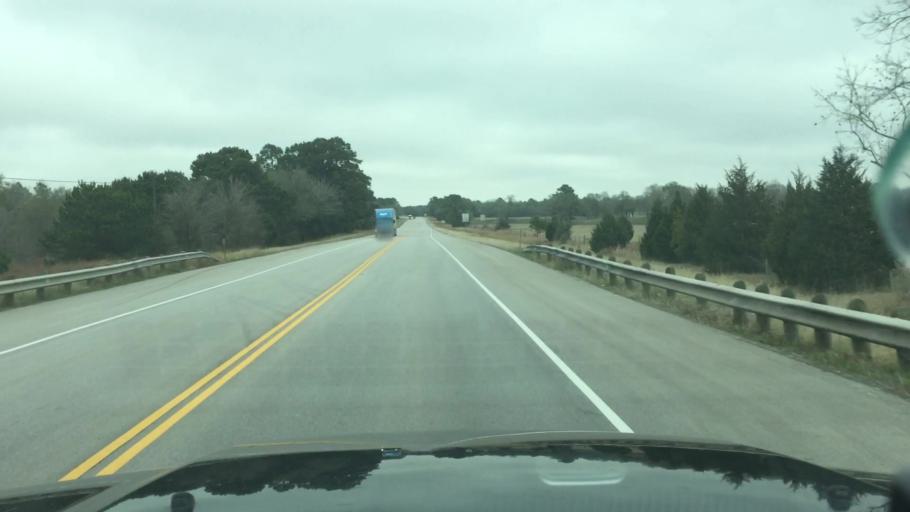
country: US
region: Texas
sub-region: Lee County
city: Giddings
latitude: 30.0848
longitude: -96.9162
